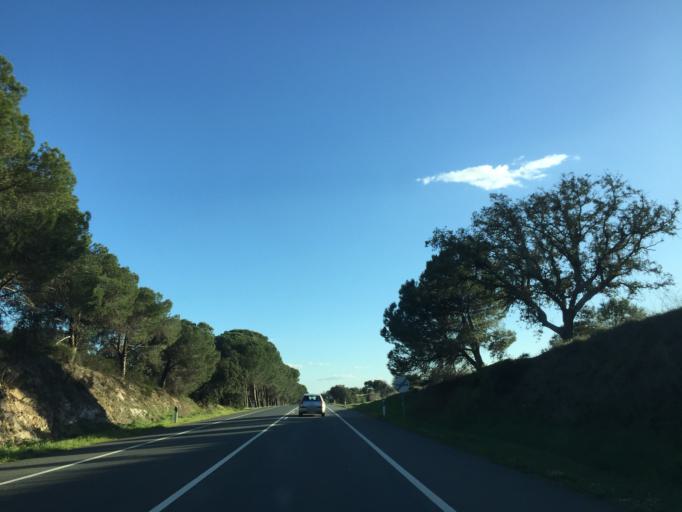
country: PT
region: Setubal
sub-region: Grandola
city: Grandola
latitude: 38.0858
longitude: -8.4176
